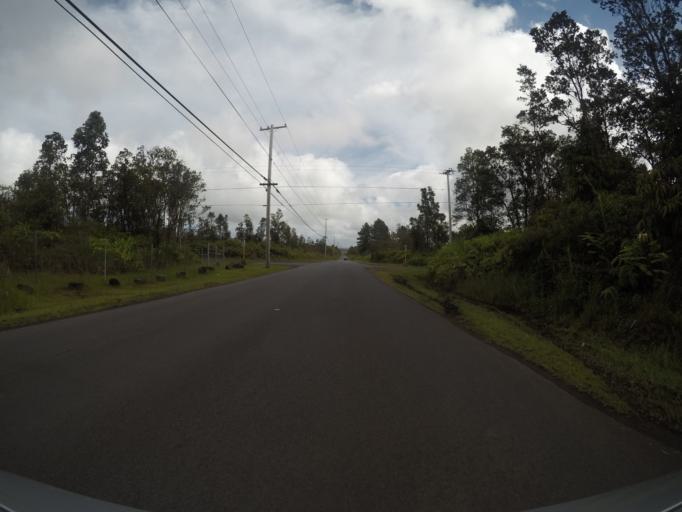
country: US
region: Hawaii
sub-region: Hawaii County
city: Fern Acres
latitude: 19.4728
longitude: -155.1387
